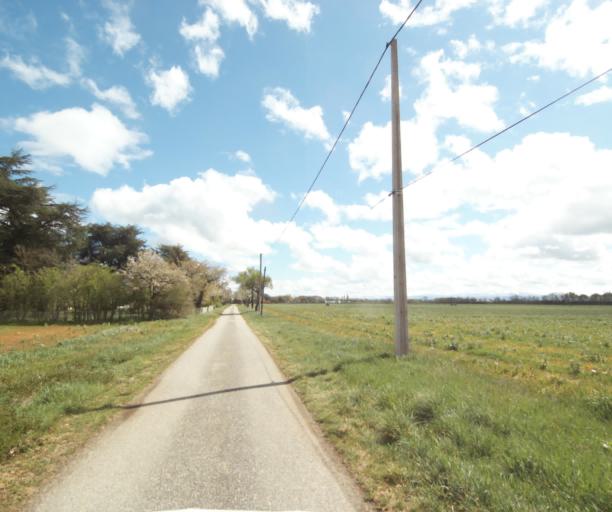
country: FR
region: Midi-Pyrenees
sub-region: Departement de l'Ariege
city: Saverdun
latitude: 43.2662
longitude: 1.5906
